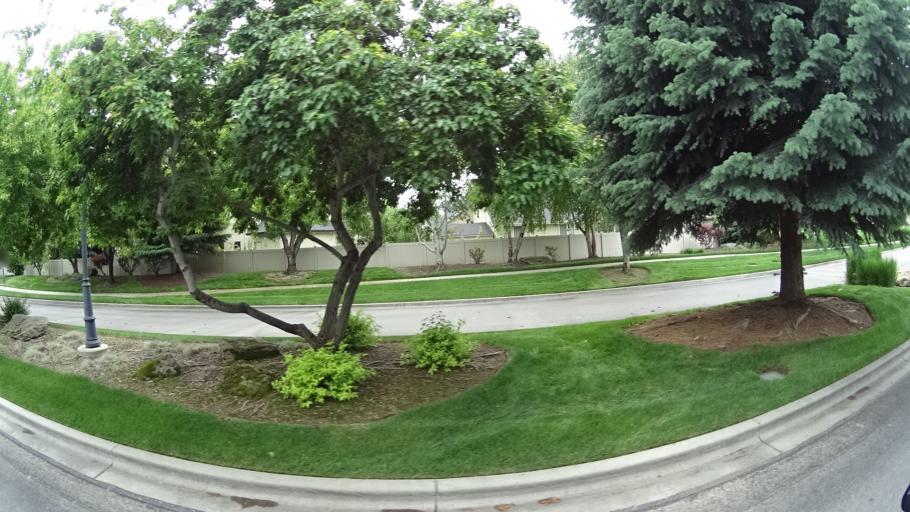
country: US
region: Idaho
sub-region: Ada County
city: Meridian
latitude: 43.6432
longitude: -116.4106
